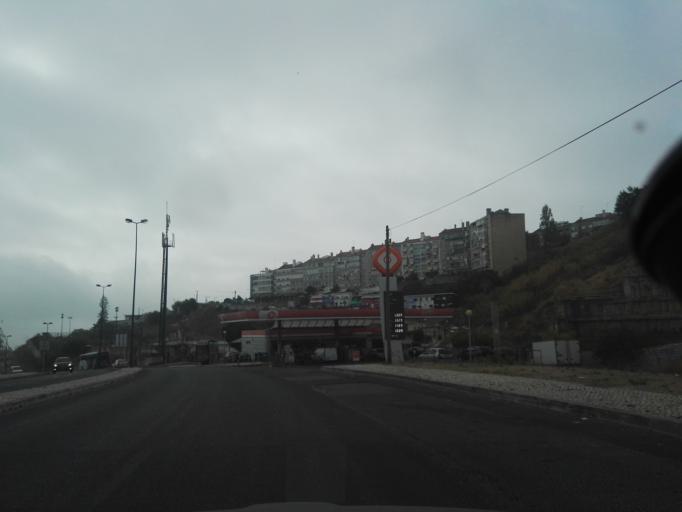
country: PT
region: Lisbon
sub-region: Lisbon
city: Lisbon
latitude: 38.7233
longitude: -9.1220
